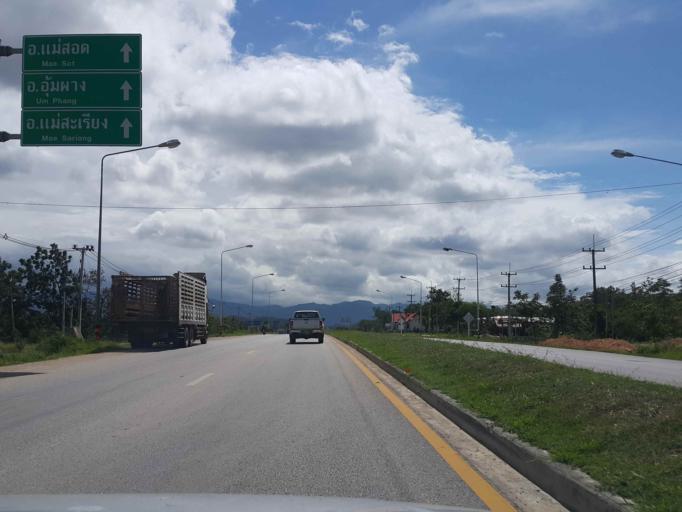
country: TH
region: Tak
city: Tak
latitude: 16.8403
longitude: 99.1116
